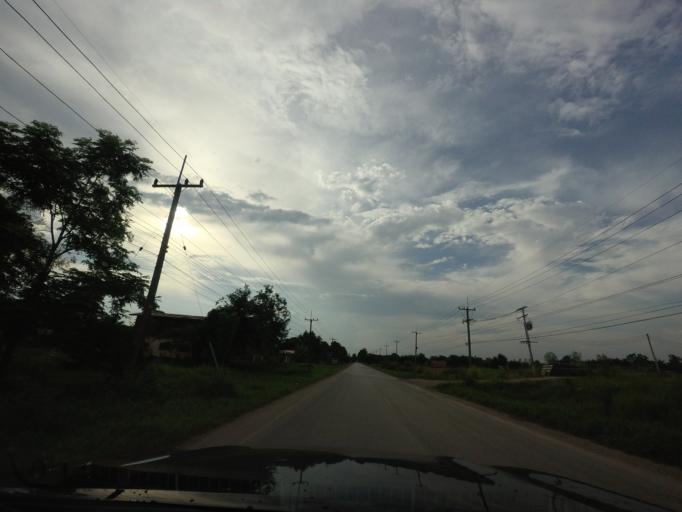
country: TH
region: Changwat Udon Thani
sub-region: Amphoe Ban Phue
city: Ban Phue
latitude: 17.7089
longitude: 102.4220
